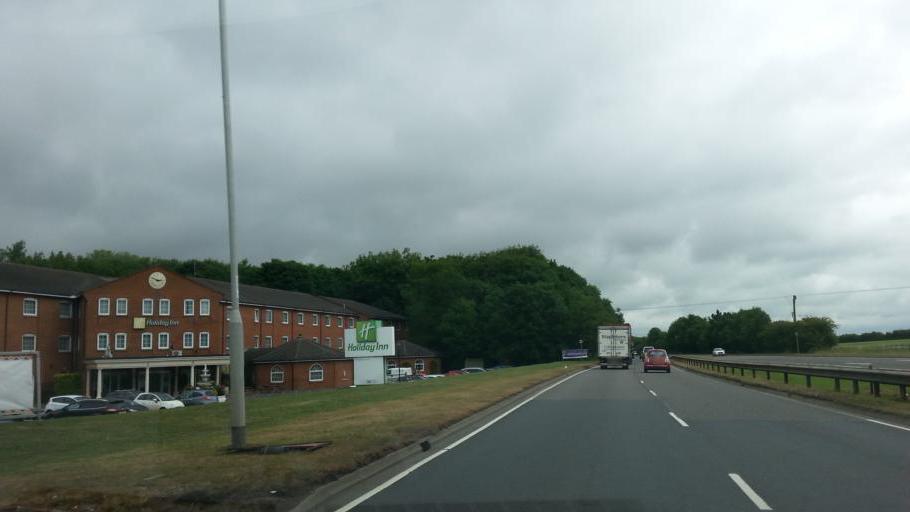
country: GB
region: England
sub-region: Northamptonshire
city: Corby
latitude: 52.4816
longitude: -0.6592
